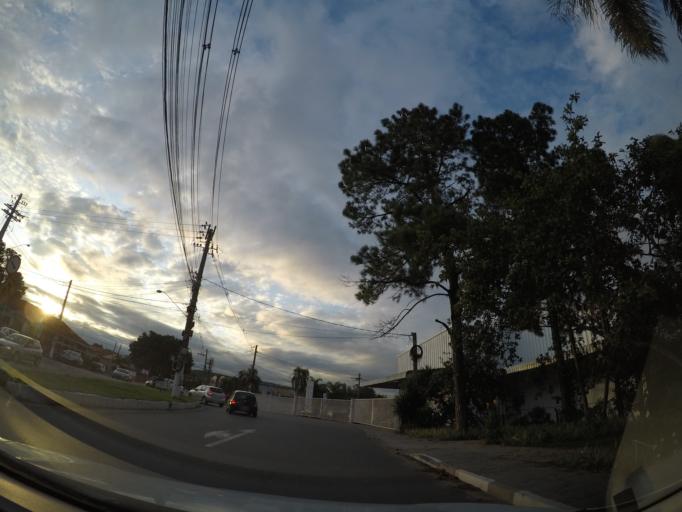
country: BR
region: Sao Paulo
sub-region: Itupeva
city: Itupeva
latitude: -23.1489
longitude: -47.0278
